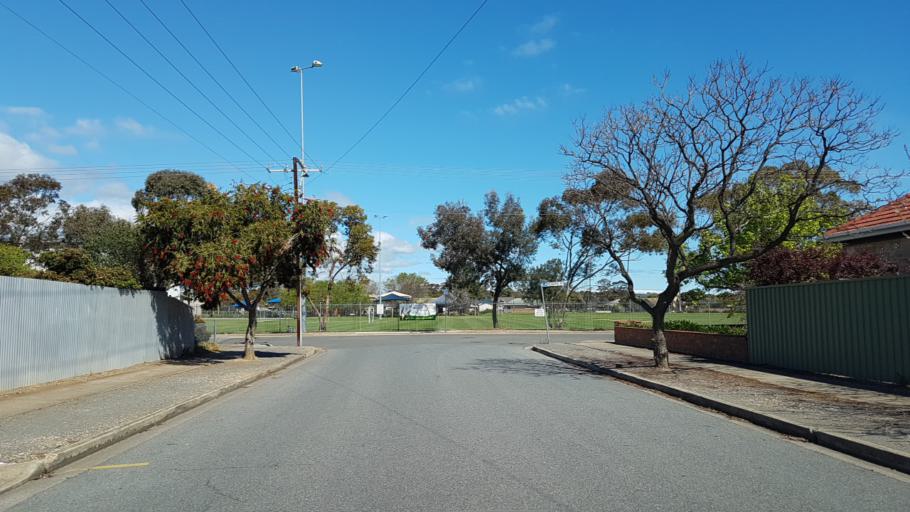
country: AU
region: South Australia
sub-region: Marion
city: Plympton Park
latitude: -34.9897
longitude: 138.5536
